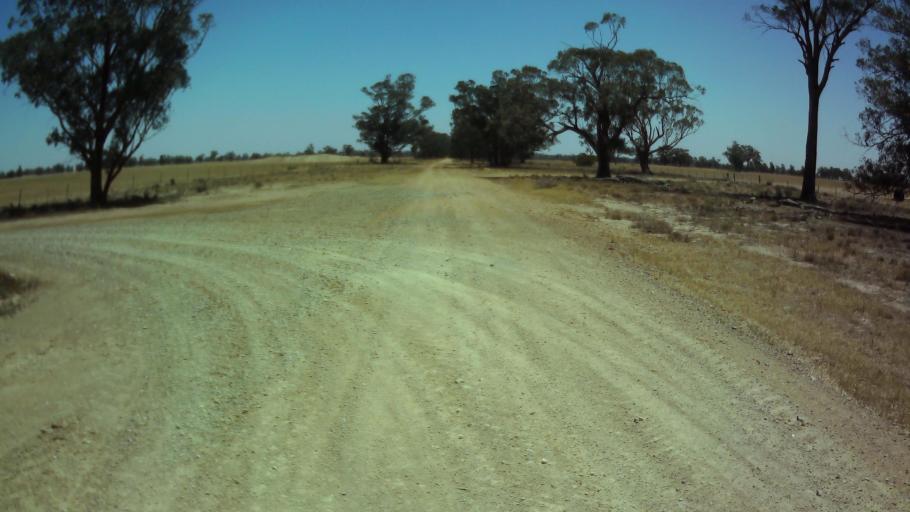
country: AU
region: New South Wales
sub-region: Weddin
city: Grenfell
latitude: -34.0320
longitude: 147.8655
